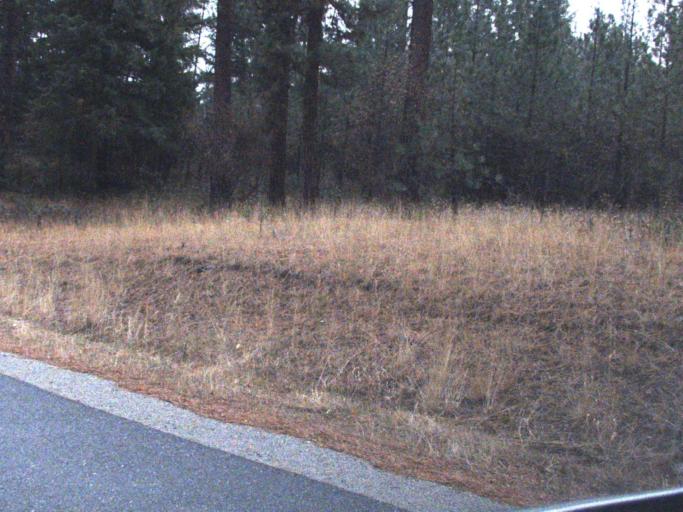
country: US
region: Washington
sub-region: Stevens County
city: Kettle Falls
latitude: 48.6060
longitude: -118.0784
